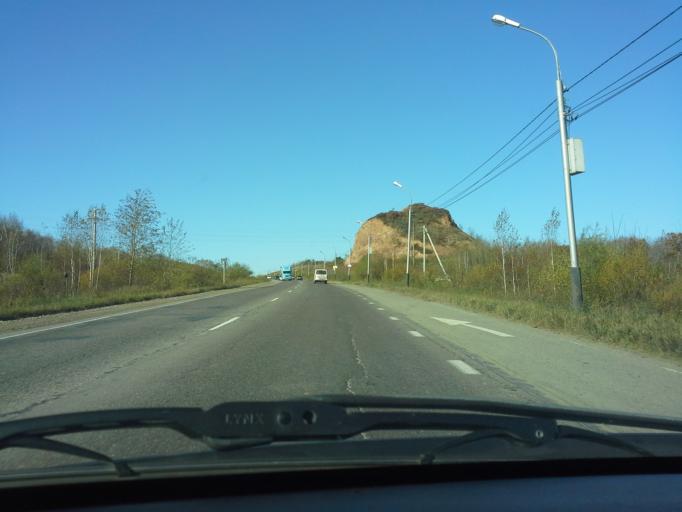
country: RU
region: Khabarovsk Krai
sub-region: Khabarovskiy Rayon
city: Khabarovsk
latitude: 48.5498
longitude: 135.0845
